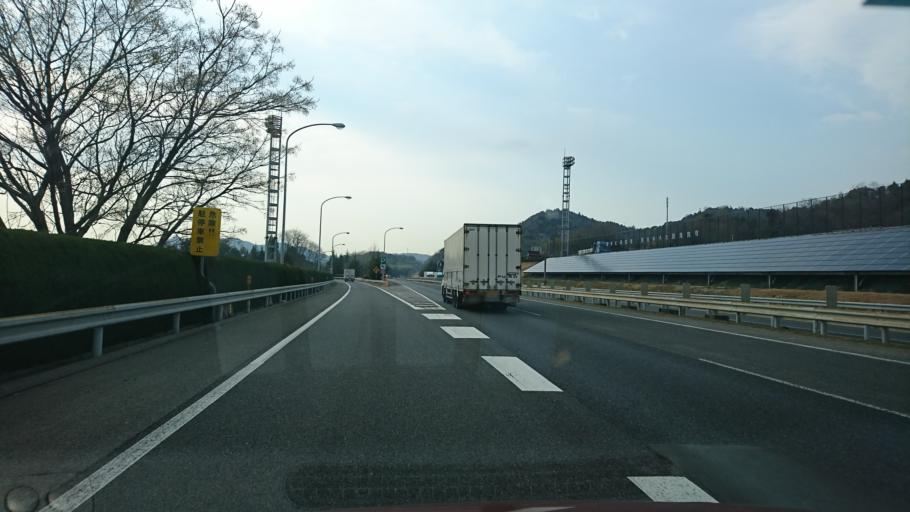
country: JP
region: Hiroshima
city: Fukuyama
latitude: 34.4916
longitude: 133.3155
